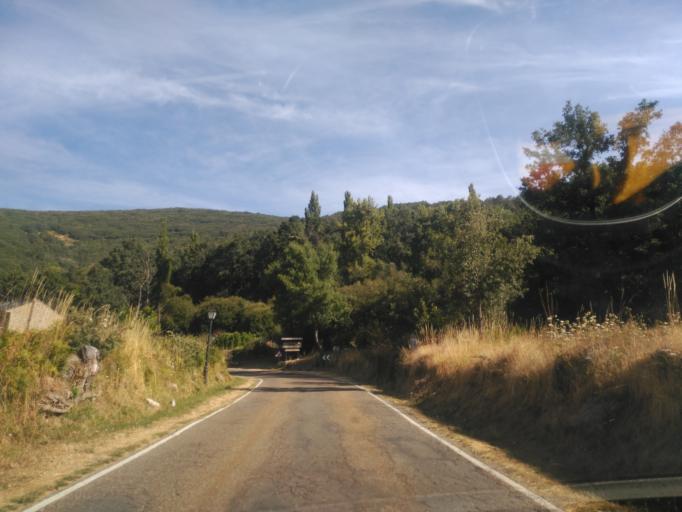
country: ES
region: Castille and Leon
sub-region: Provincia de Zamora
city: Galende
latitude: 42.1368
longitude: -6.7160
